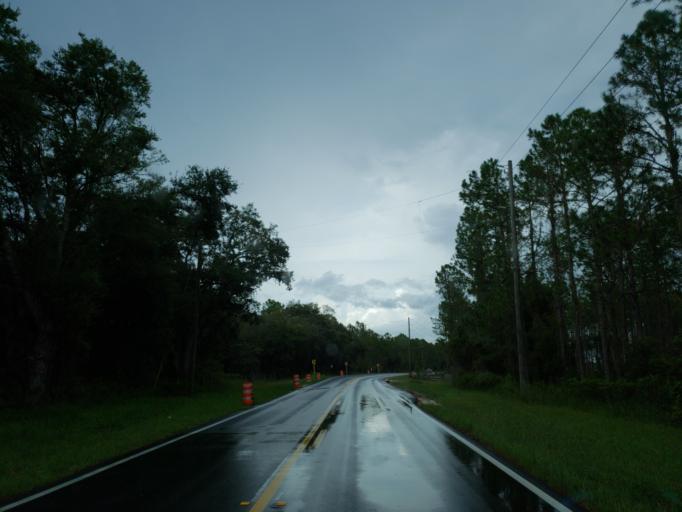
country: US
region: Florida
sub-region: Pasco County
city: Land O' Lakes
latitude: 28.3152
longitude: -82.4206
